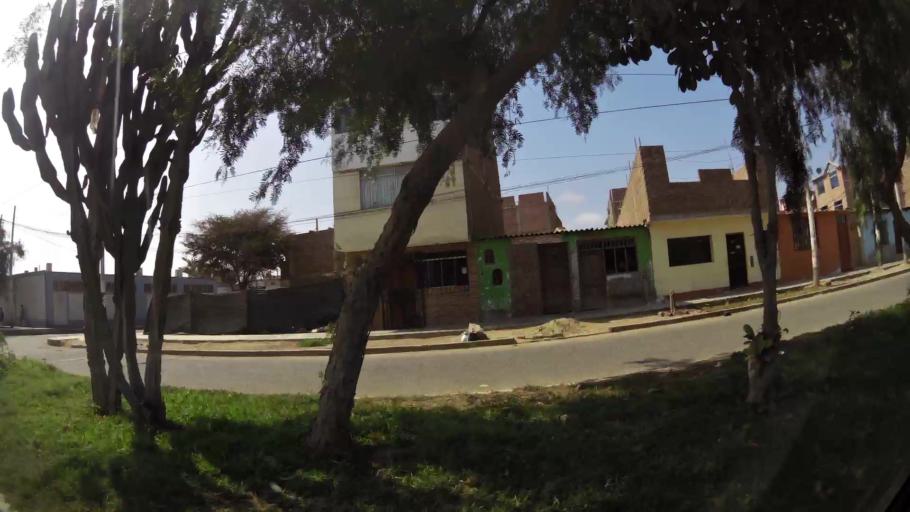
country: PE
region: La Libertad
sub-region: Provincia de Trujillo
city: Buenos Aires
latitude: -8.1330
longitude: -79.0489
